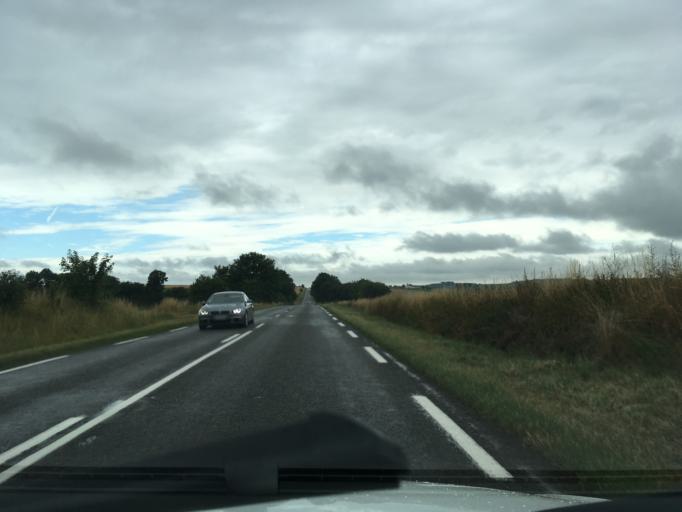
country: FR
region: Picardie
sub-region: Departement de l'Aisne
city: Origny-Sainte-Benoite
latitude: 49.8524
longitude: 3.5235
